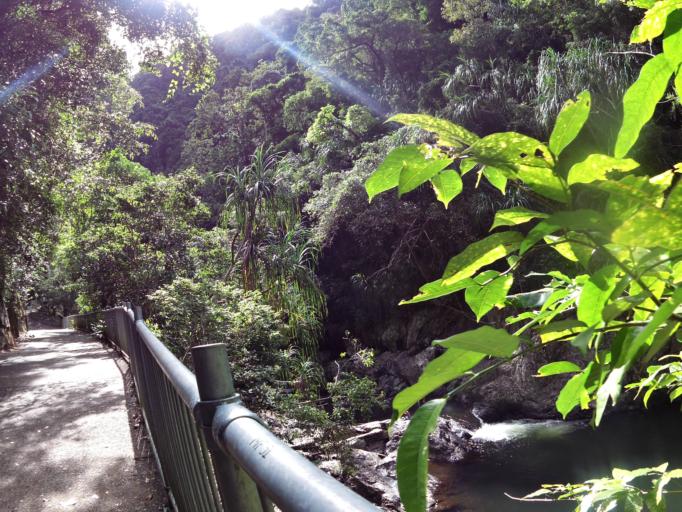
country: AU
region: Queensland
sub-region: Cairns
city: Woree
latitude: -16.9642
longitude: 145.6712
